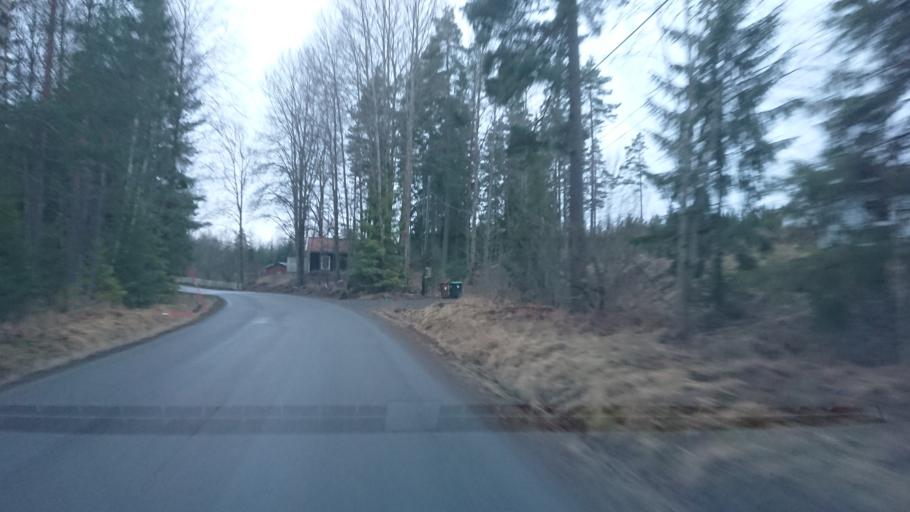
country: SE
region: Uppsala
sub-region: Osthammars Kommun
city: Bjorklinge
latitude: 59.9965
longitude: 17.5953
